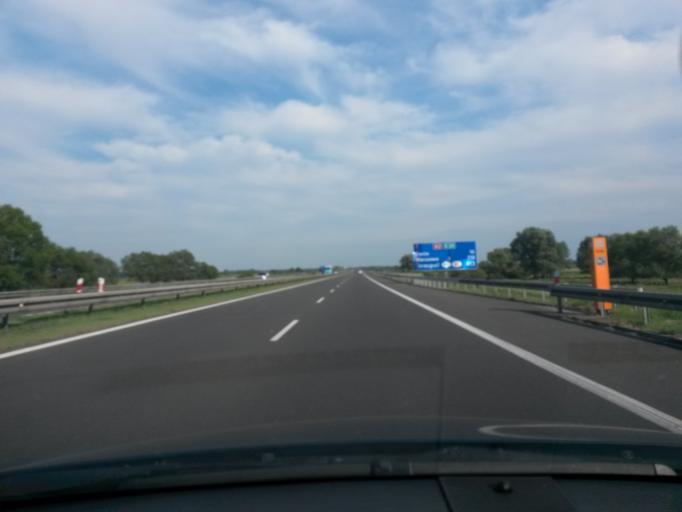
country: PL
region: Greater Poland Voivodeship
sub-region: Powiat koninski
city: Rzgow Pierwszy
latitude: 52.2018
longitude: 18.0318
